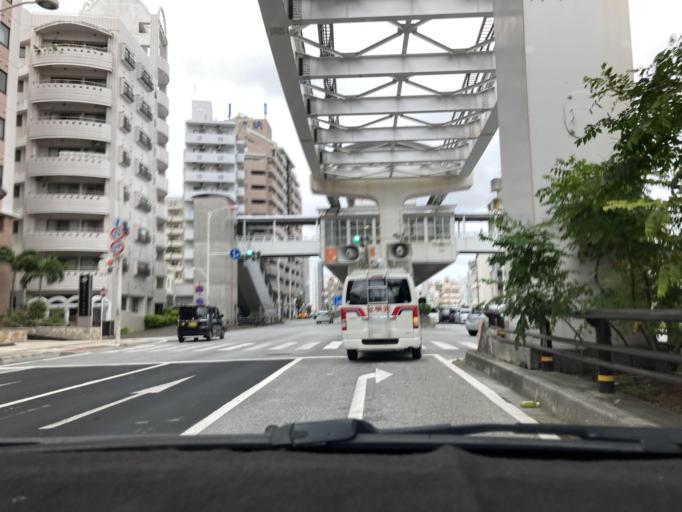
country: JP
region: Okinawa
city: Naha-shi
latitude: 26.2162
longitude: 127.6954
